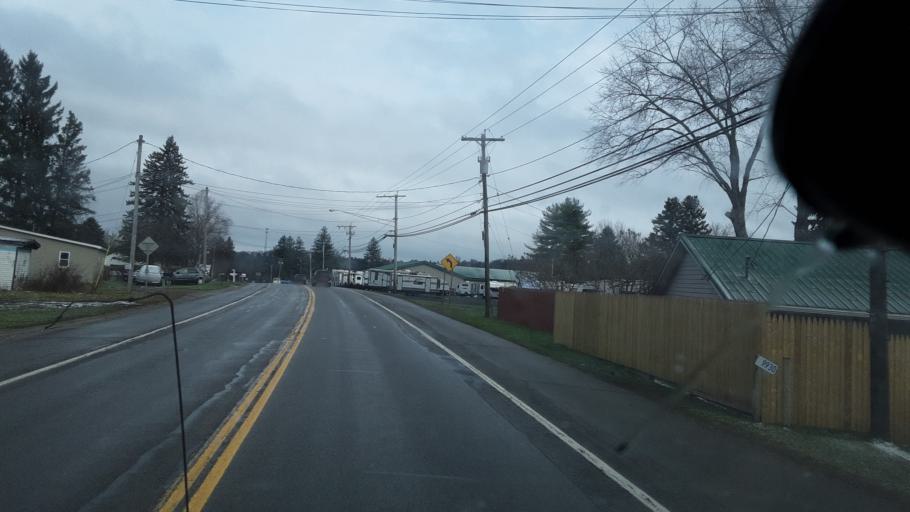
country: US
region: New York
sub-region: Cattaraugus County
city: Delevan
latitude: 42.4311
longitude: -78.4825
